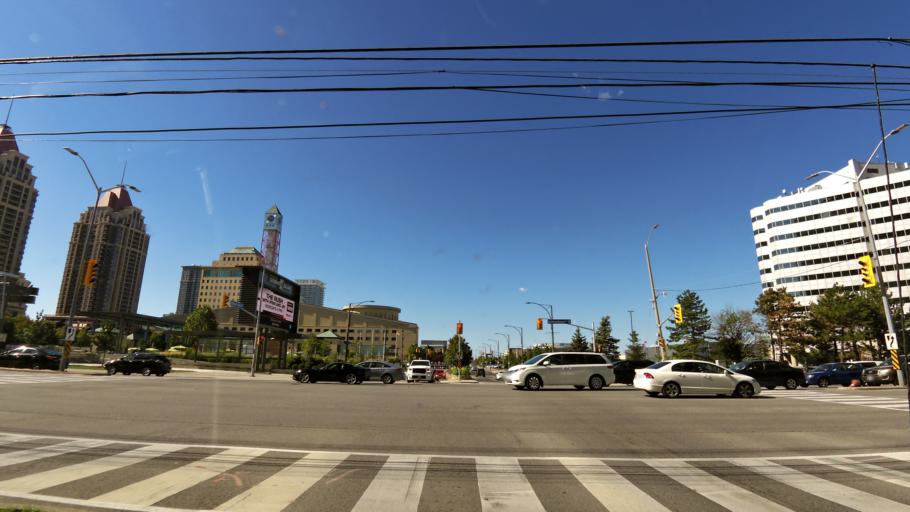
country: CA
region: Ontario
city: Mississauga
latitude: 43.5881
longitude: -79.6414
